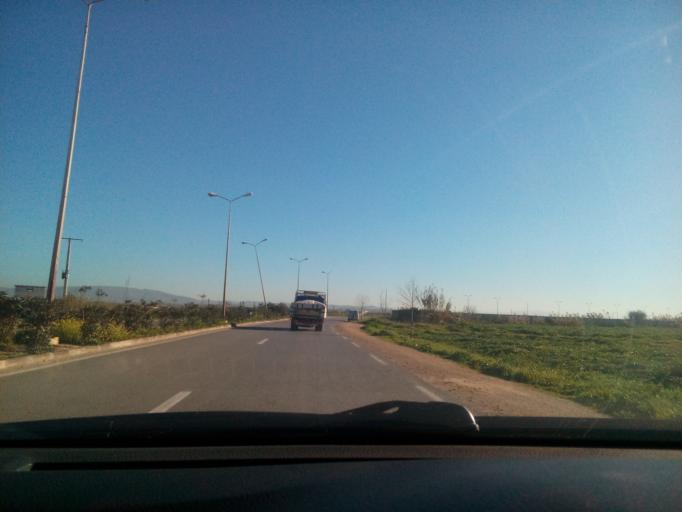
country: DZ
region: Relizane
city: Relizane
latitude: 35.7539
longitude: 0.6151
